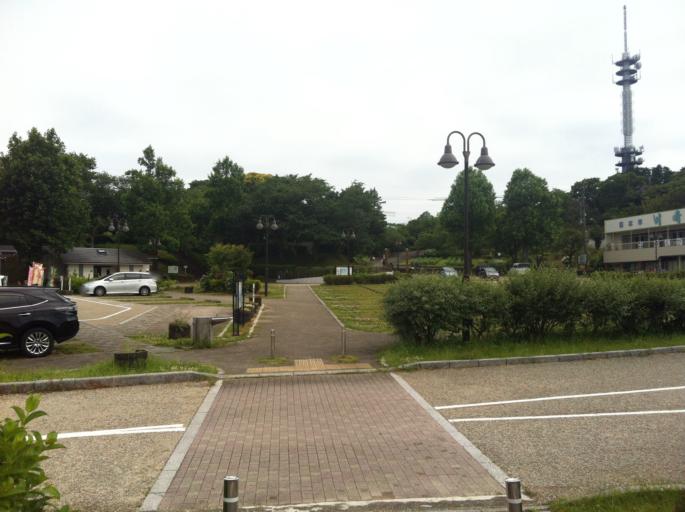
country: JP
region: Shizuoka
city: Shizuoka-shi
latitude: 34.9767
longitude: 138.4666
